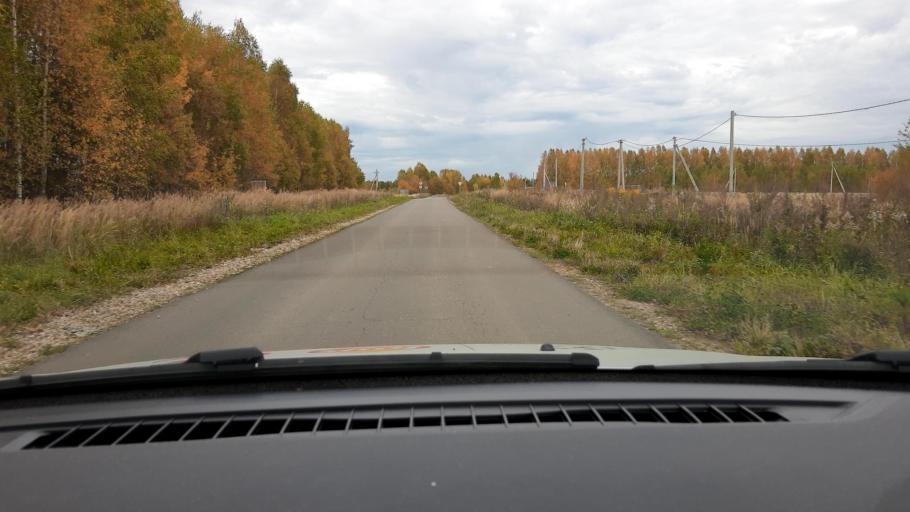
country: RU
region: Nizjnij Novgorod
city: Babino
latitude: 56.1320
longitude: 43.6448
